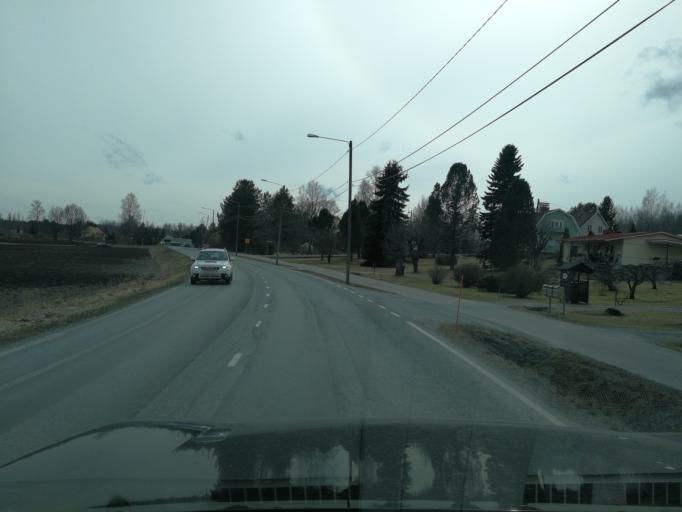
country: FI
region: Uusimaa
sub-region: Helsinki
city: Lohja
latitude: 60.2002
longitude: 24.0048
